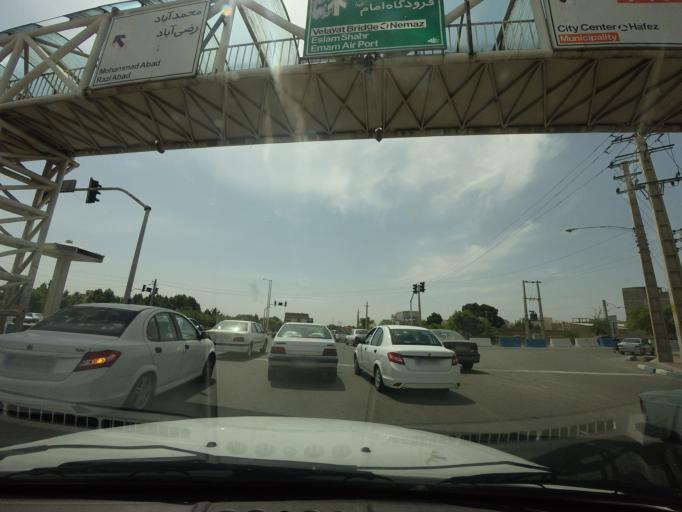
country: IR
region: Tehran
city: Shahriar
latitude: 35.6694
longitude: 51.0690
